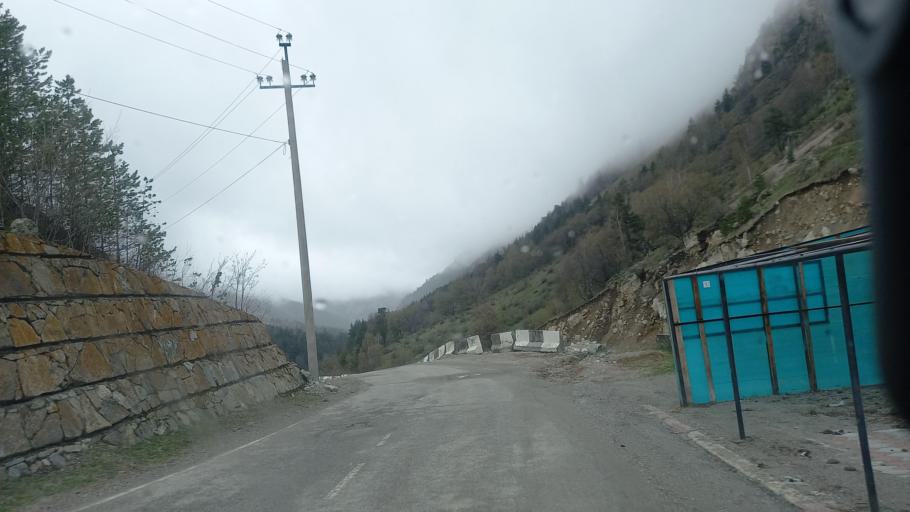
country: RU
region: Kabardino-Balkariya
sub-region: El'brusskiy Rayon
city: El'brus
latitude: 43.2283
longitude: 42.6576
